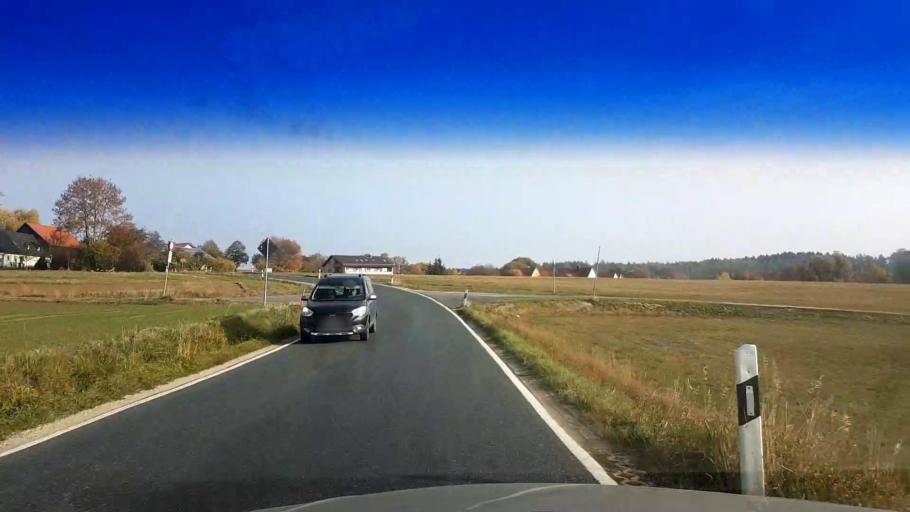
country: DE
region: Bavaria
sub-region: Upper Franconia
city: Stadelhofen
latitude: 50.0166
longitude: 11.2010
